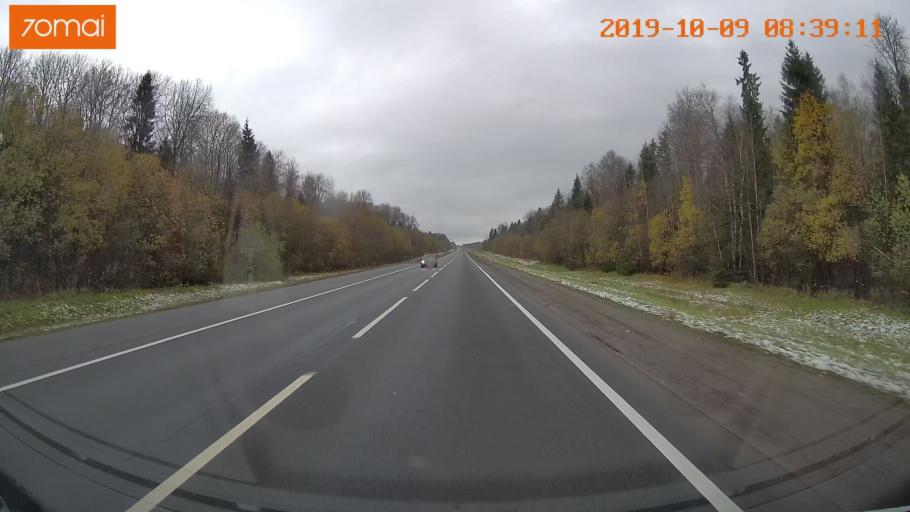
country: RU
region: Vologda
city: Gryazovets
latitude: 58.9675
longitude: 40.1564
